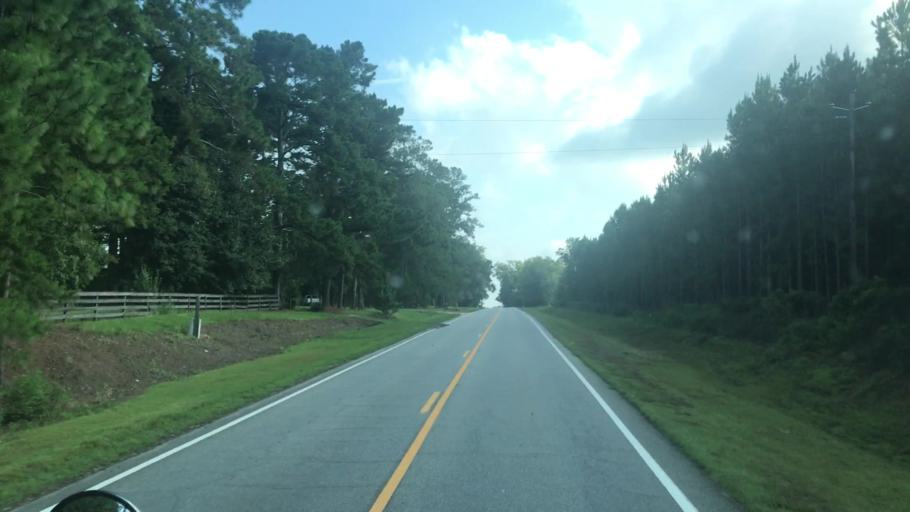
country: US
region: Florida
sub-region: Gadsden County
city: Havana
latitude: 30.7675
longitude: -84.4881
